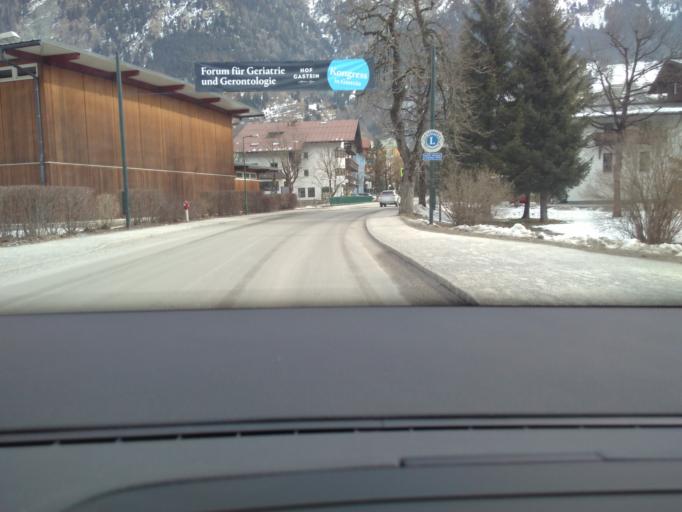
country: AT
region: Salzburg
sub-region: Politischer Bezirk Sankt Johann im Pongau
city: Bad Hofgastein
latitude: 47.1701
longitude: 13.0995
